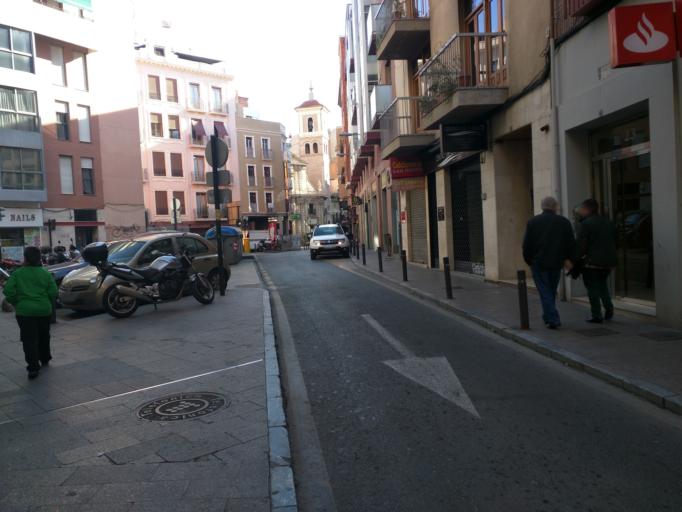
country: ES
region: Murcia
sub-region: Murcia
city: Murcia
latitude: 37.9845
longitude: -1.1344
